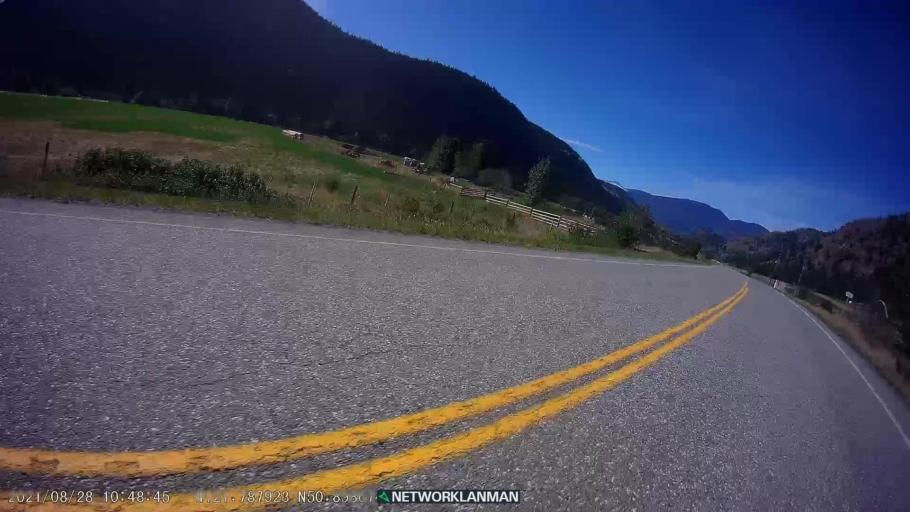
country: CA
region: British Columbia
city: Lillooet
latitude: 50.8993
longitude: -121.7888
